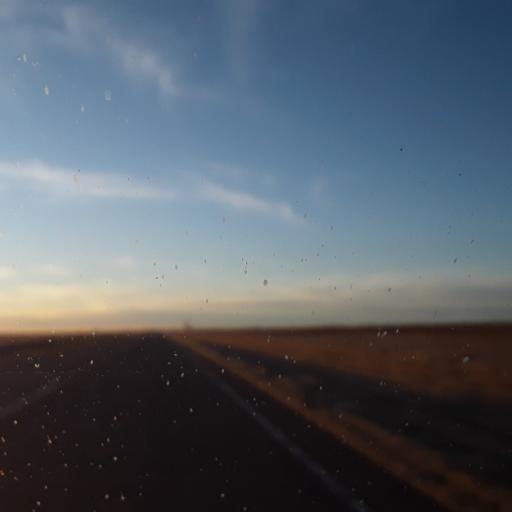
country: US
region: Colorado
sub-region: Cheyenne County
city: Cheyenne Wells
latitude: 38.8170
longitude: -102.5122
